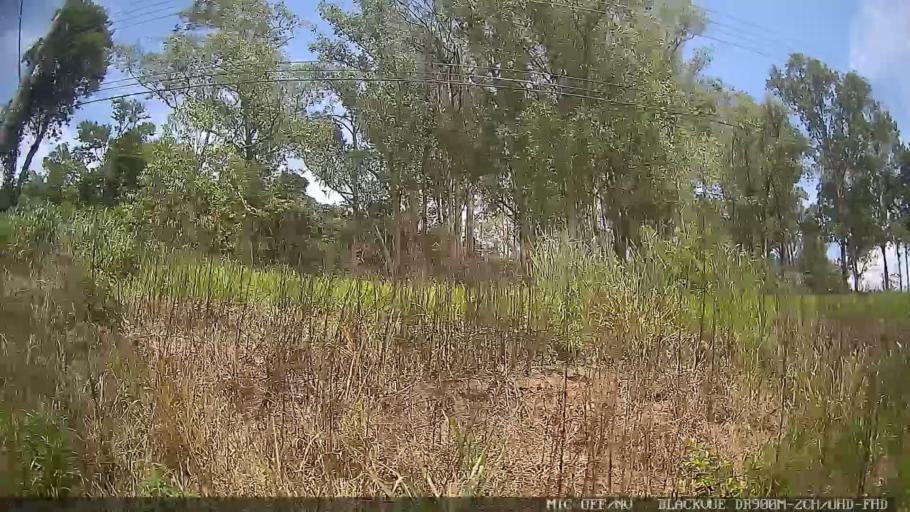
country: BR
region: Sao Paulo
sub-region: Santa Isabel
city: Santa Isabel
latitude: -23.3641
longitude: -46.1843
